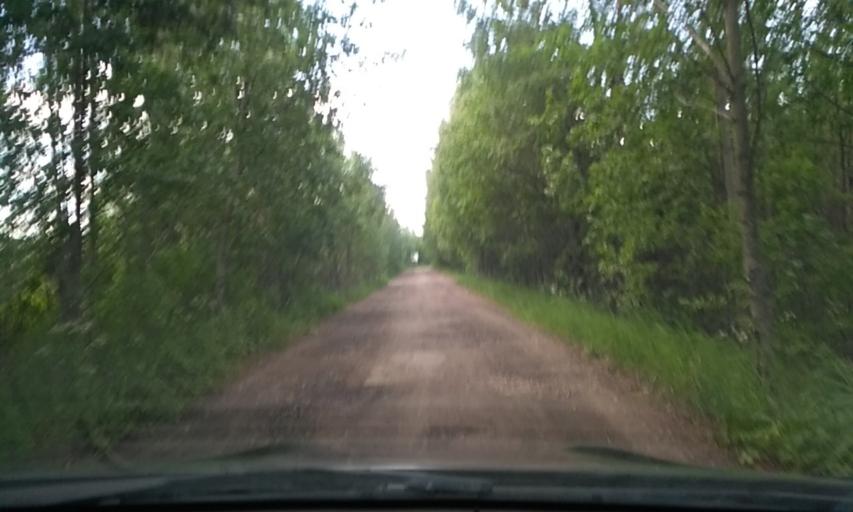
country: RU
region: Leningrad
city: Otradnoye
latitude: 59.8114
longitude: 30.8268
